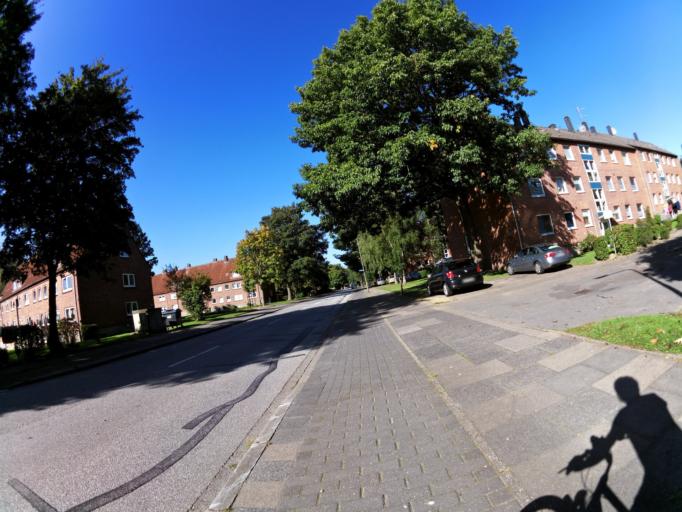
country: DE
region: Schleswig-Holstein
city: Eckernforde
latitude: 54.4543
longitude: 9.8422
